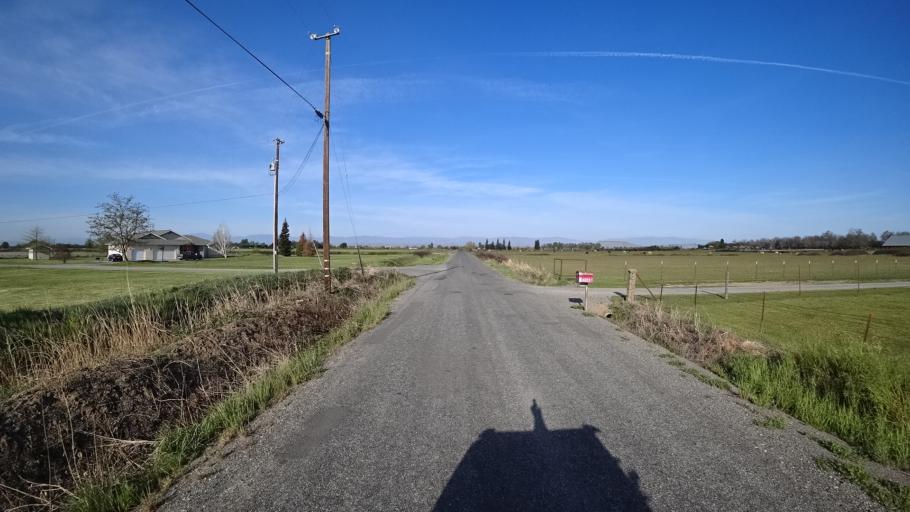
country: US
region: California
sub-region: Glenn County
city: Orland
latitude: 39.7152
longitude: -122.2286
